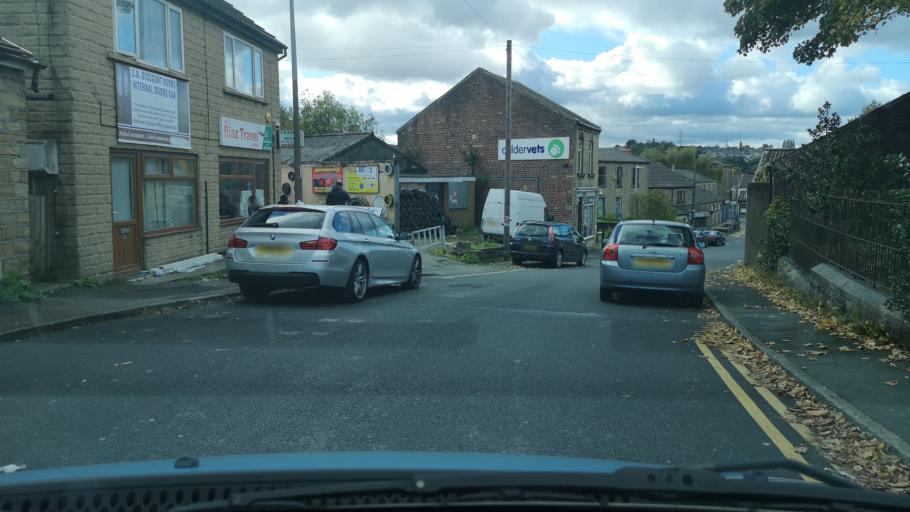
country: GB
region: England
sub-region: Kirklees
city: Heckmondwike
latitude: 53.7071
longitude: -1.6723
